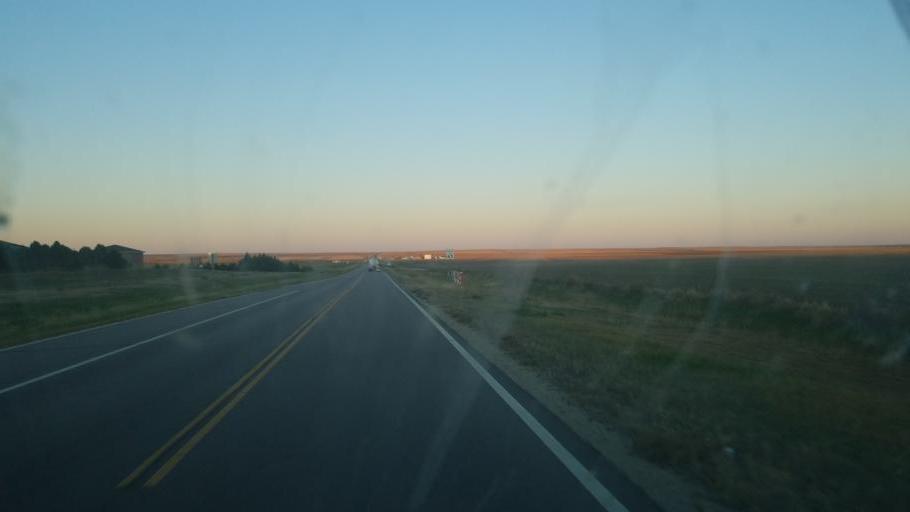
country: US
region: Kansas
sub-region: Wallace County
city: Sharon Springs
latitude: 38.9018
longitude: -101.7566
